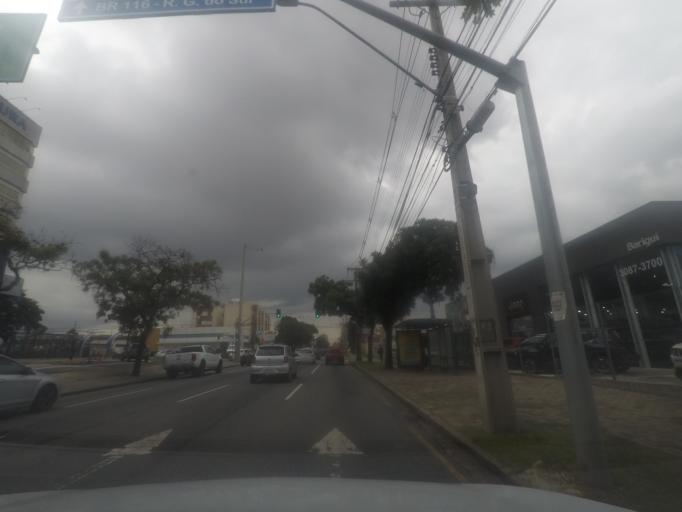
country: BR
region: Parana
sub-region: Curitiba
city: Curitiba
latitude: -25.4789
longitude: -49.2957
